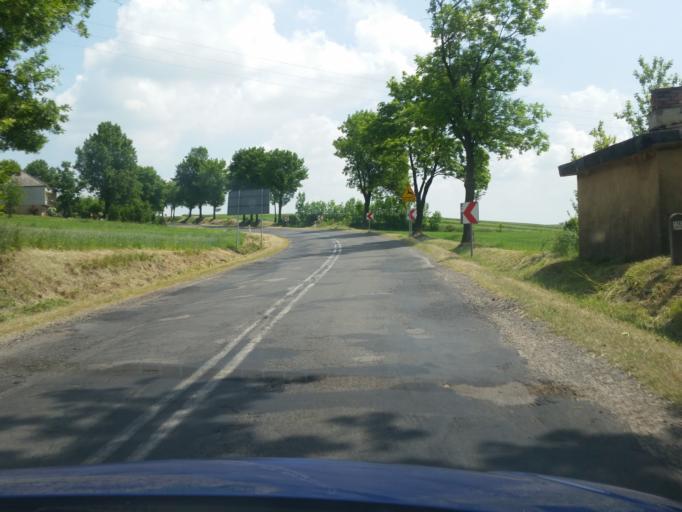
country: PL
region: Swietokrzyskie
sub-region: Powiat pinczowski
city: Dzialoszyce
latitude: 50.3245
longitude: 20.2767
